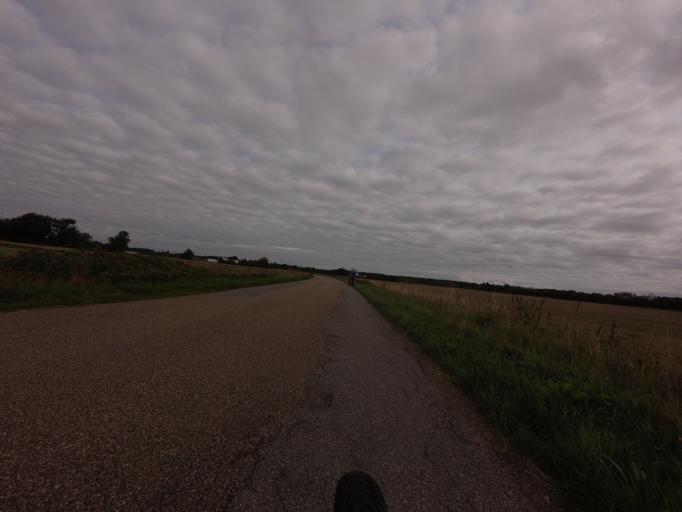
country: DK
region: North Denmark
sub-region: Hjorring Kommune
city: Hirtshals
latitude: 57.5682
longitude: 10.0328
